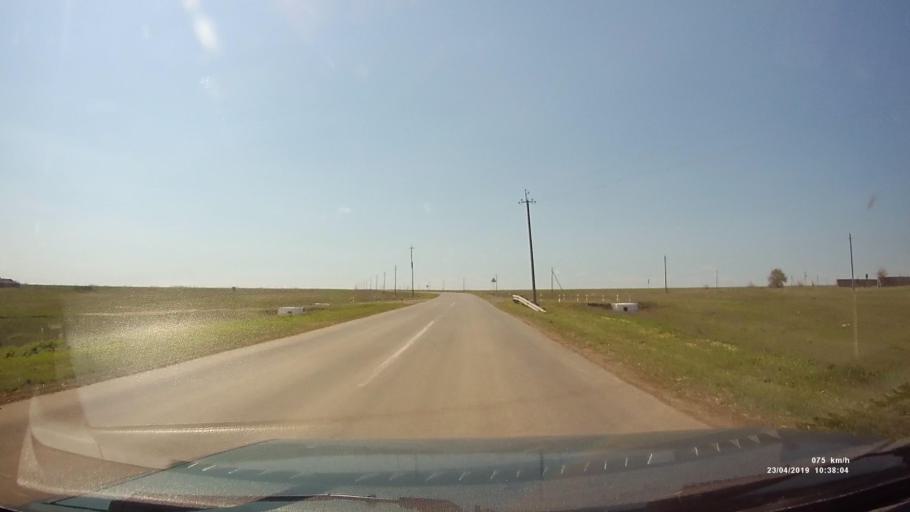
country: RU
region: Kalmykiya
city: Yashalta
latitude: 46.5372
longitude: 42.6393
